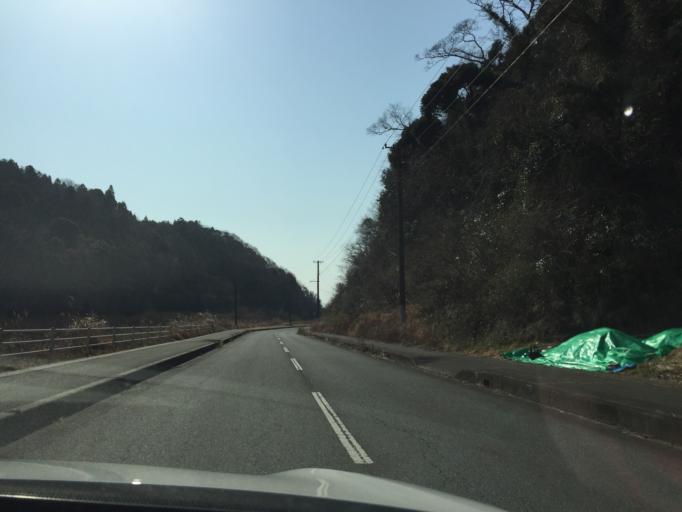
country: JP
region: Fukushima
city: Iwaki
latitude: 36.9598
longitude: 140.9338
